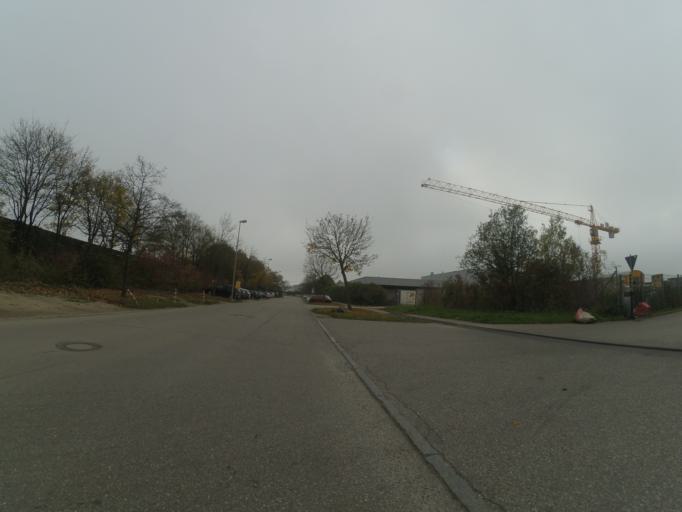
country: DE
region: Baden-Wuerttemberg
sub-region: Tuebingen Region
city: Erbach
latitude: 48.3510
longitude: 9.9315
